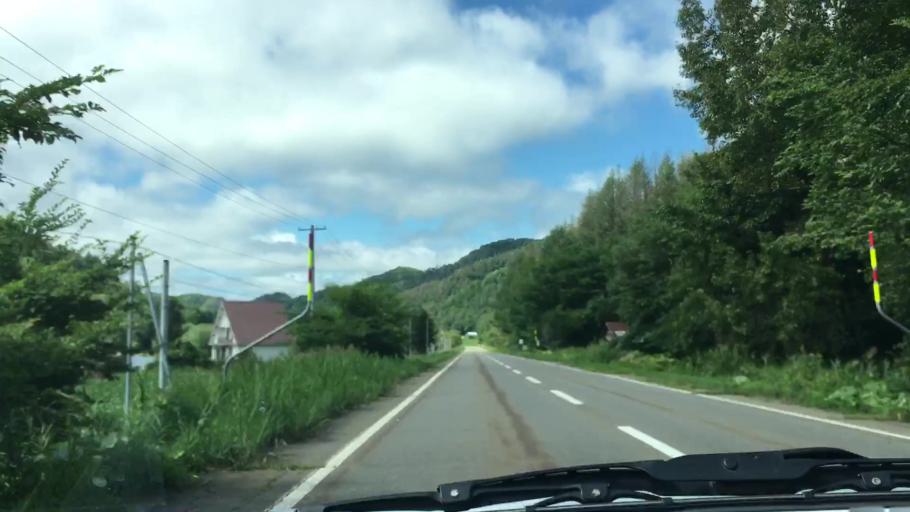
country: JP
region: Hokkaido
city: Kitami
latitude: 43.3602
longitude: 143.8397
